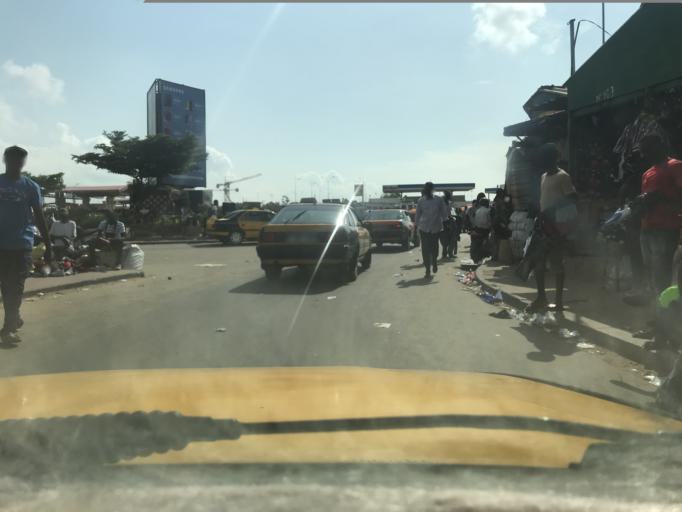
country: SN
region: Dakar
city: Dakar
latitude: 14.6978
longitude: -17.4444
